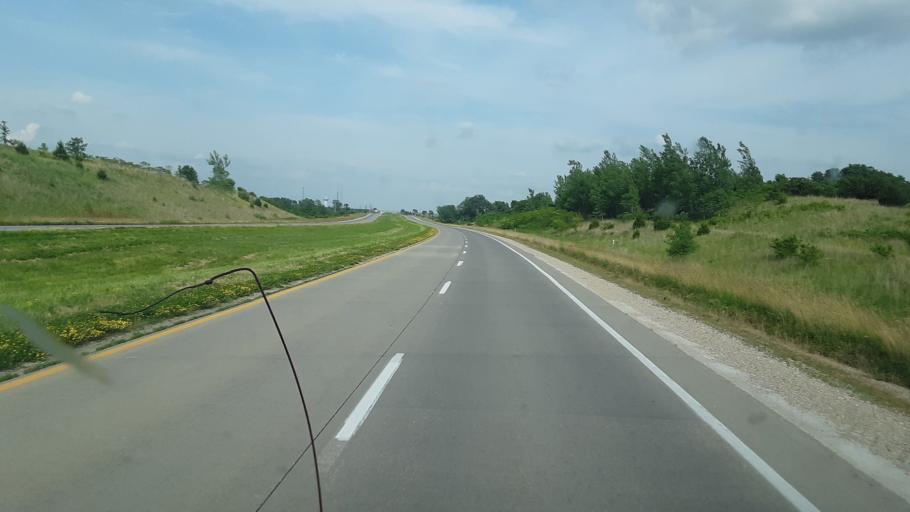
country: US
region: Iowa
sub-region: Marshall County
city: Marshalltown
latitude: 42.0035
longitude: -92.9696
